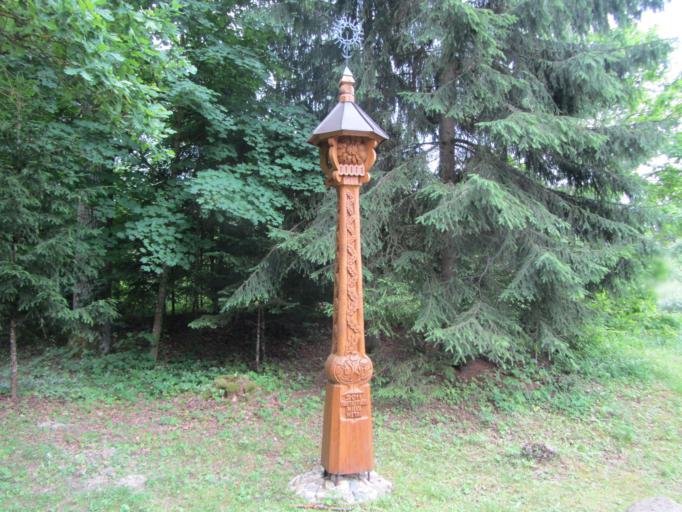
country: LT
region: Vilnius County
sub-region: Vilniaus Rajonas
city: Vievis
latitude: 54.8333
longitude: 24.9514
